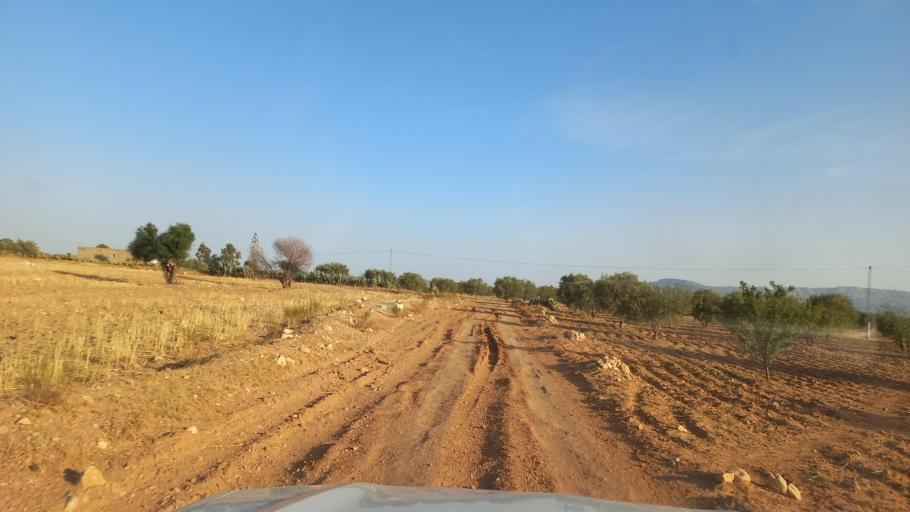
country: TN
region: Al Qasrayn
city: Kasserine
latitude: 35.2572
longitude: 8.9074
